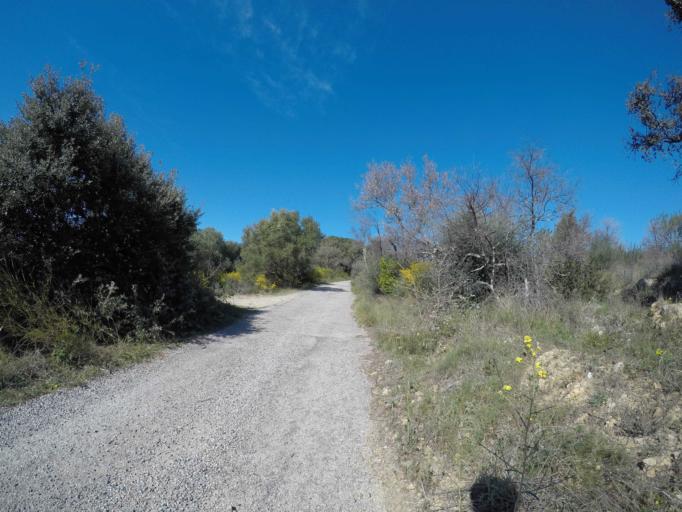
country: FR
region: Languedoc-Roussillon
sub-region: Departement des Pyrenees-Orientales
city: Millas
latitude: 42.7032
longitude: 2.6801
